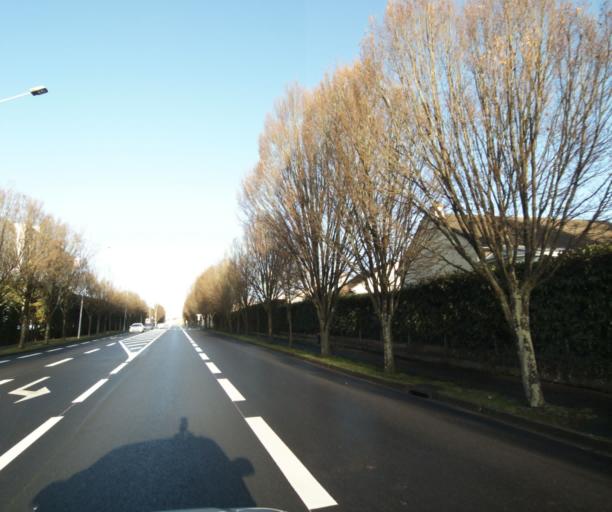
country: FR
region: Pays de la Loire
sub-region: Departement de la Sarthe
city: Coulaines
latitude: 48.0151
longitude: 0.2209
